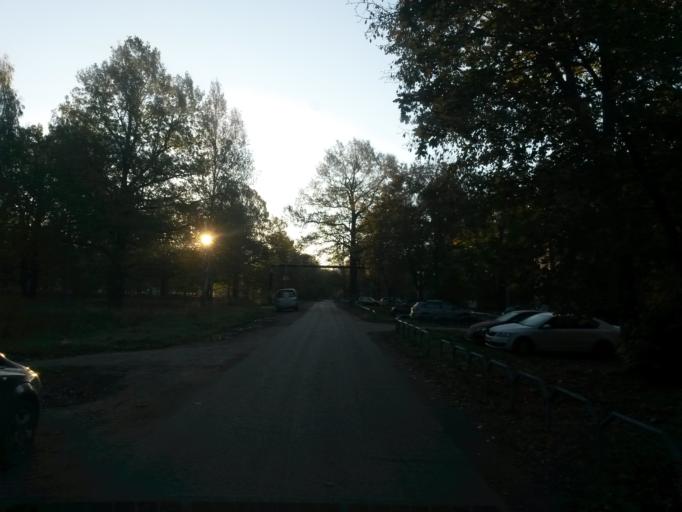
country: RU
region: Moskovskaya
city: Lyubuchany
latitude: 55.2448
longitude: 37.6307
